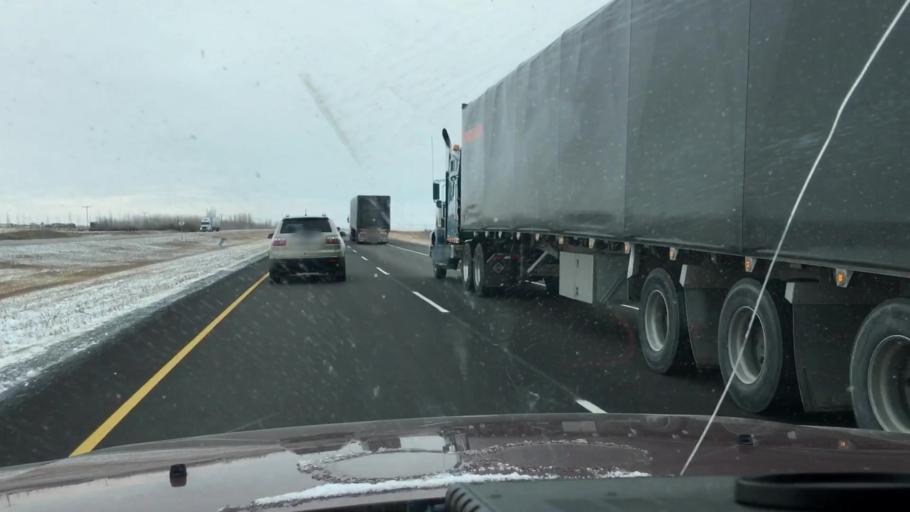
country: CA
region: Saskatchewan
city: Saskatoon
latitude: 51.7769
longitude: -106.4764
